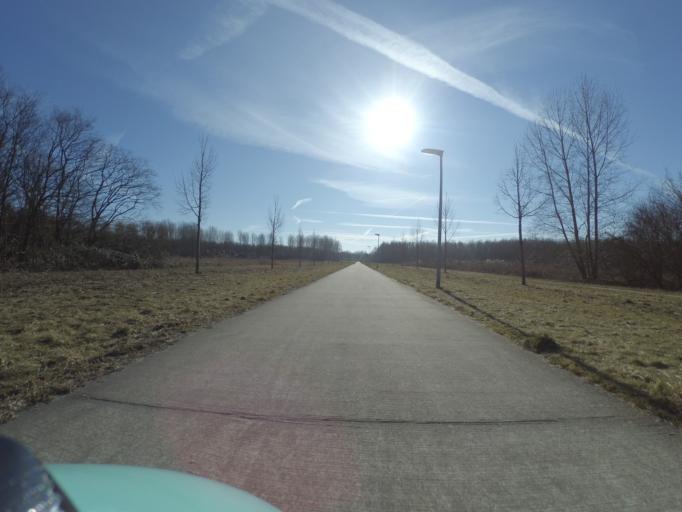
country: NL
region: Flevoland
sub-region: Gemeente Almere
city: Almere Stad
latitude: 52.3835
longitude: 5.1760
